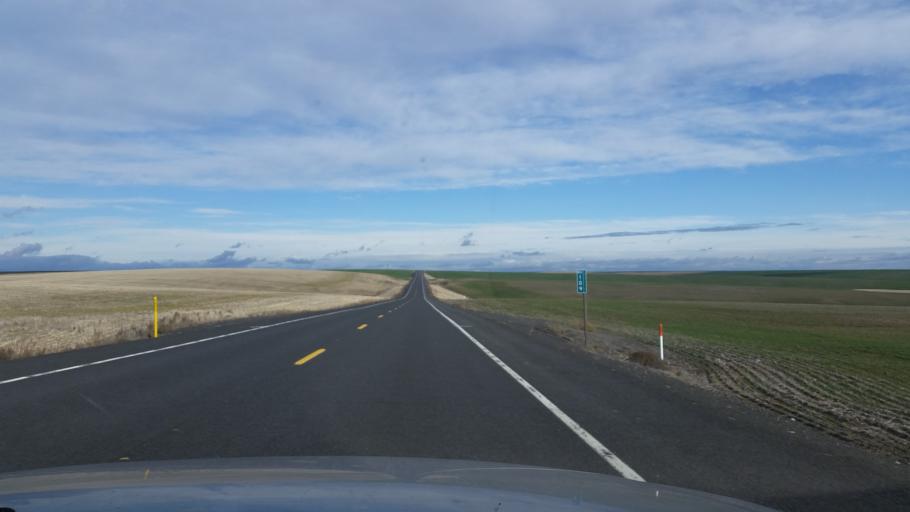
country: US
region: Washington
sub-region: Adams County
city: Ritzville
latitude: 47.3987
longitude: -118.3965
